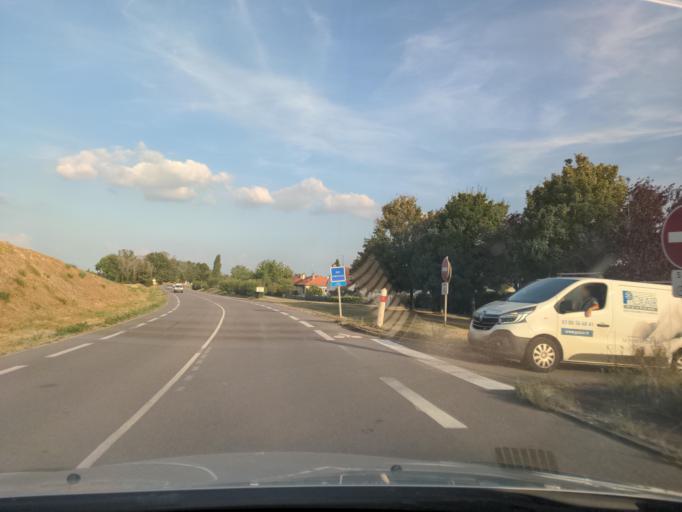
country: FR
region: Bourgogne
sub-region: Departement de la Cote-d'Or
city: Neuilly-les-Dijon
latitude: 47.2835
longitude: 5.1015
